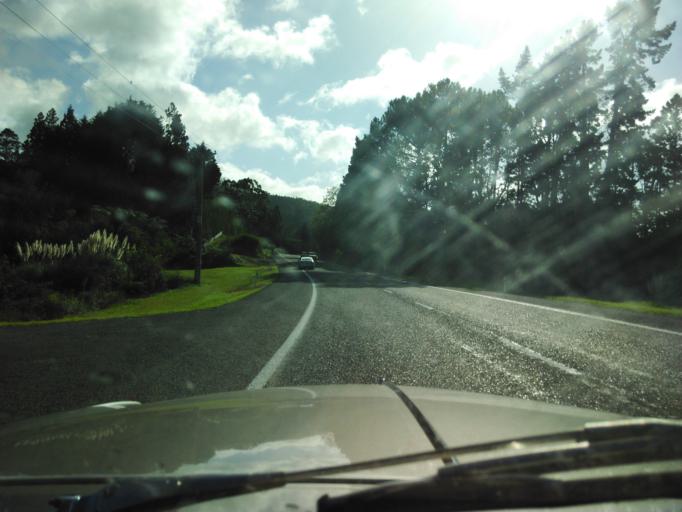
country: NZ
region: Bay of Plenty
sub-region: Western Bay of Plenty District
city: Katikati
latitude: -37.4829
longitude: 175.9310
